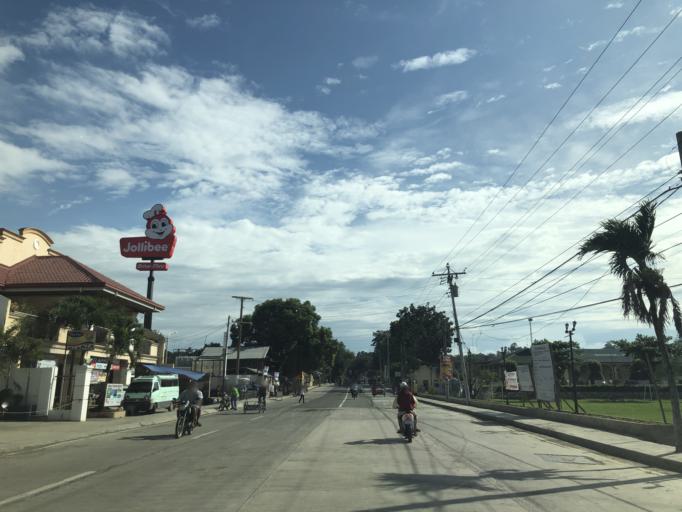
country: PH
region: Western Visayas
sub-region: Province of Iloilo
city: Maribong
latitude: 11.1227
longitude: 122.5388
